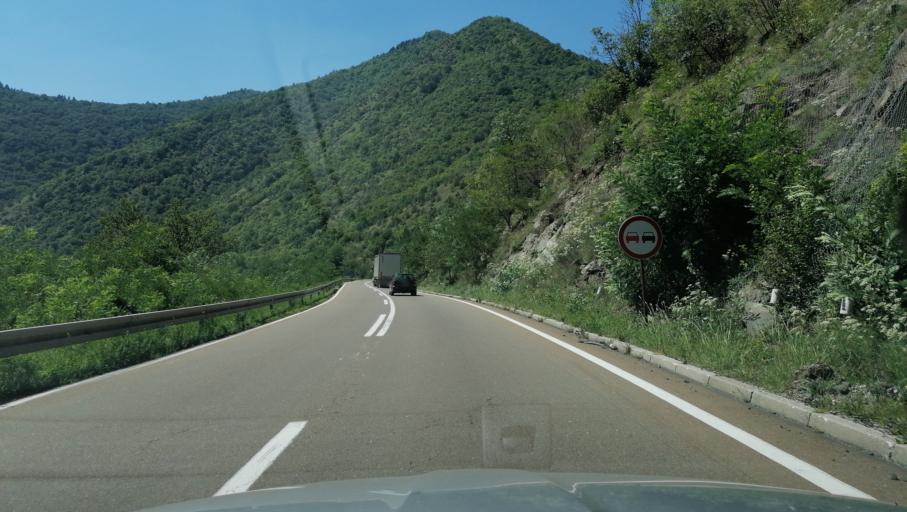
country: RS
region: Central Serbia
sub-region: Raski Okrug
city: Kraljevo
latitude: 43.5568
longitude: 20.6142
